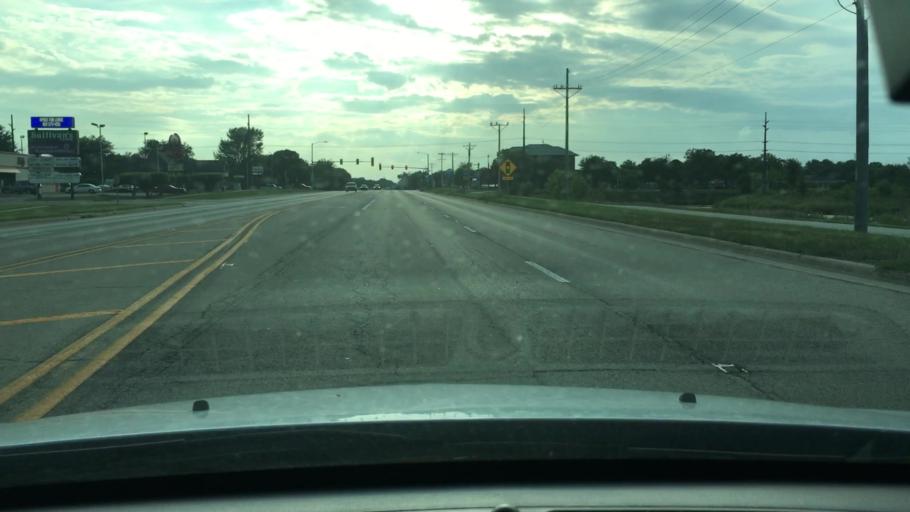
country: US
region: Illinois
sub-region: Ogle County
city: Rochelle
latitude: 41.9342
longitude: -89.0518
